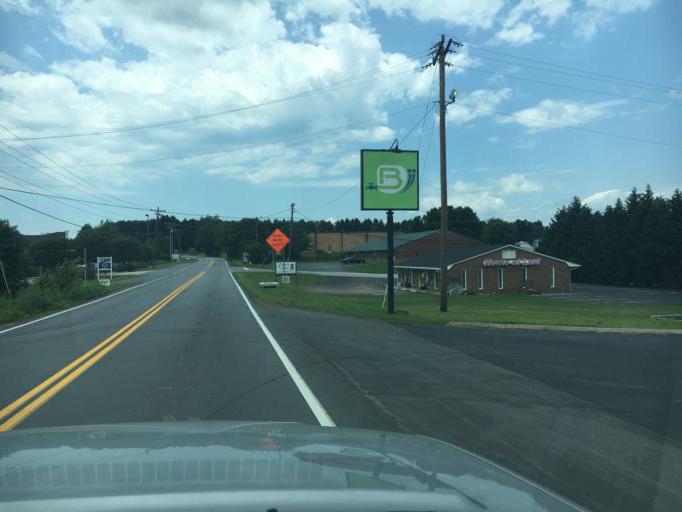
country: US
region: South Carolina
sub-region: Greenville County
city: Five Forks
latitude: 34.8696
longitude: -82.2484
